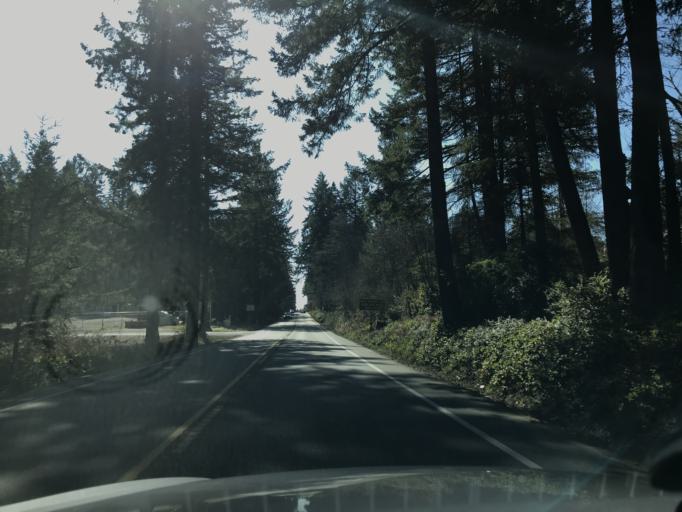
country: US
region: Washington
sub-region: Pierce County
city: Key Center
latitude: 47.3729
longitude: -122.7135
